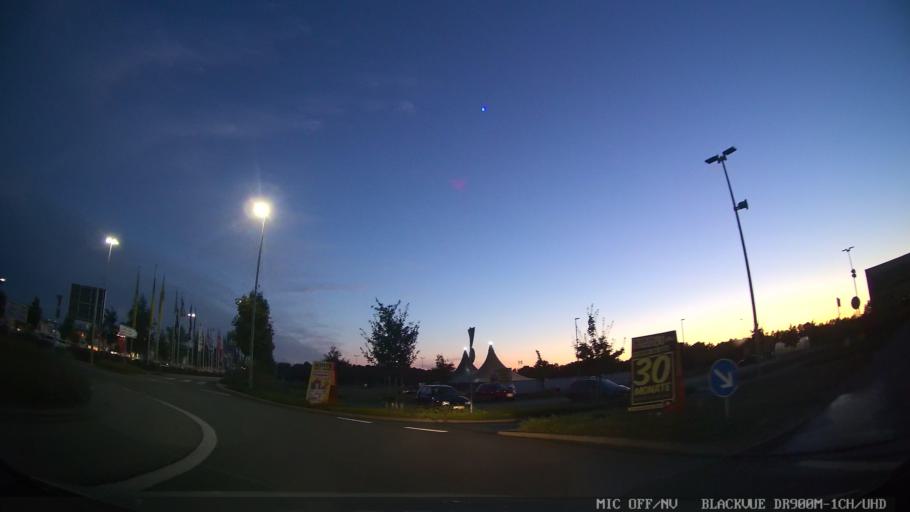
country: DE
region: Schleswig-Holstein
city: Bad Schwartau
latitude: 53.9142
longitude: 10.7314
